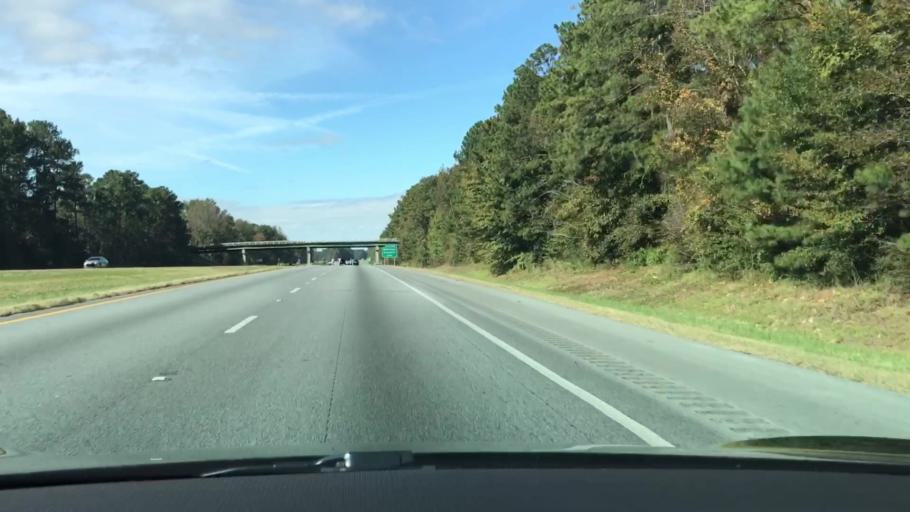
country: US
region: Georgia
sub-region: Walton County
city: Social Circle
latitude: 33.5863
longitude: -83.6075
